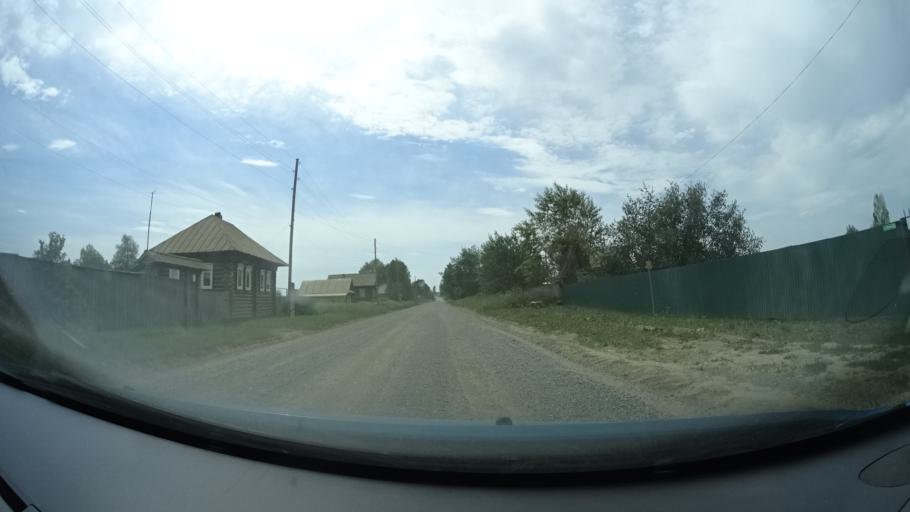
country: RU
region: Perm
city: Barda
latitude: 56.8122
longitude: 55.6667
